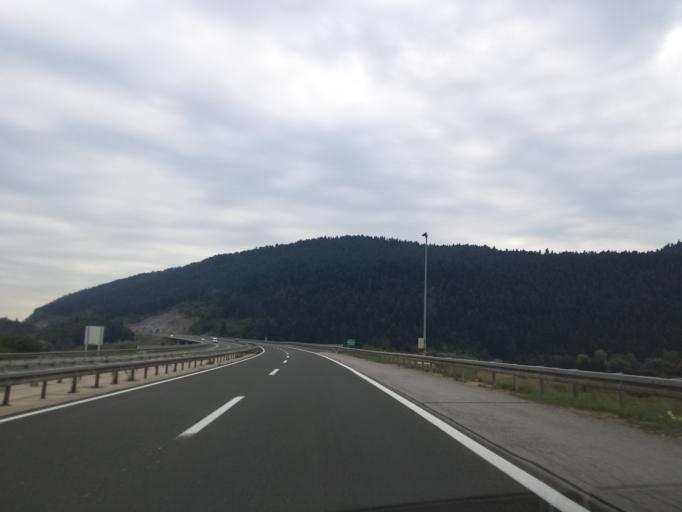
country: HR
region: Licko-Senjska
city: Otocac
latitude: 44.8649
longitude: 15.2086
